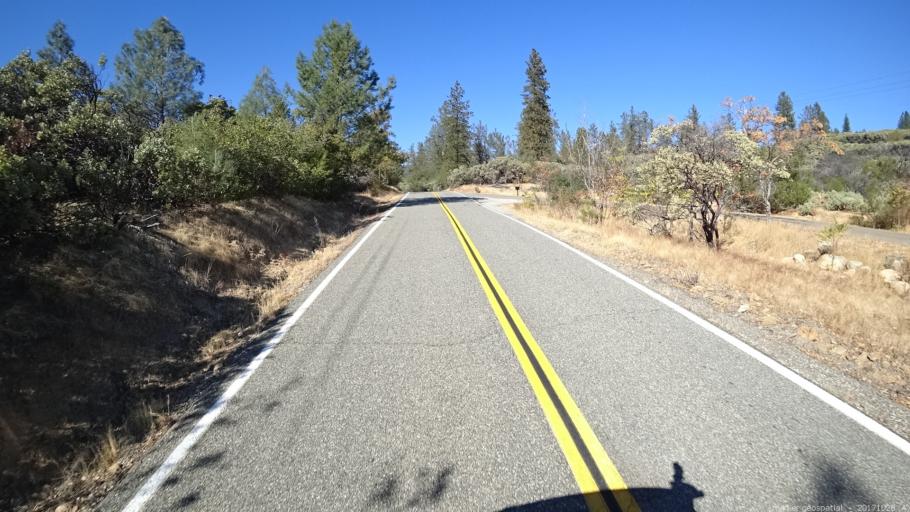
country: US
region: California
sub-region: Shasta County
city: Shasta
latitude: 40.6548
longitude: -122.4620
